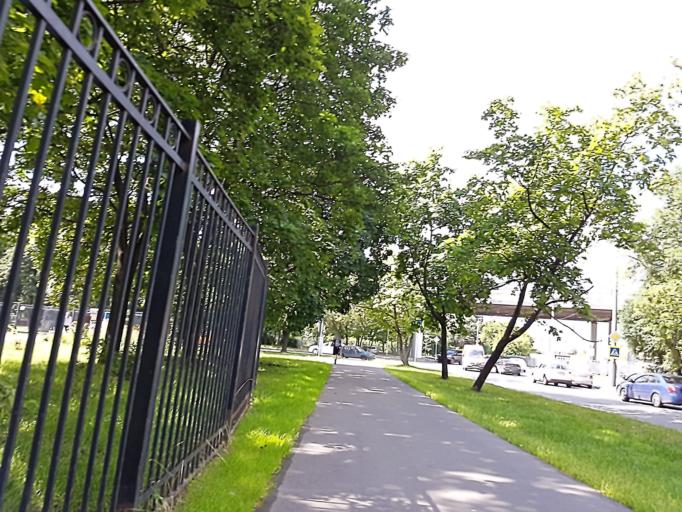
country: RU
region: Moskovskaya
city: Novogireyevo
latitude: 55.7428
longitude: 37.8169
